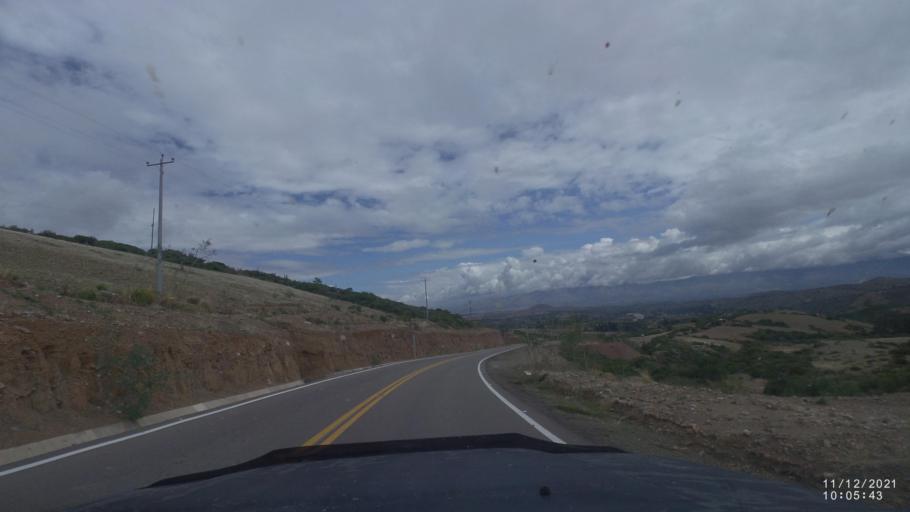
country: BO
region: Cochabamba
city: Cliza
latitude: -17.6970
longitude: -65.9475
